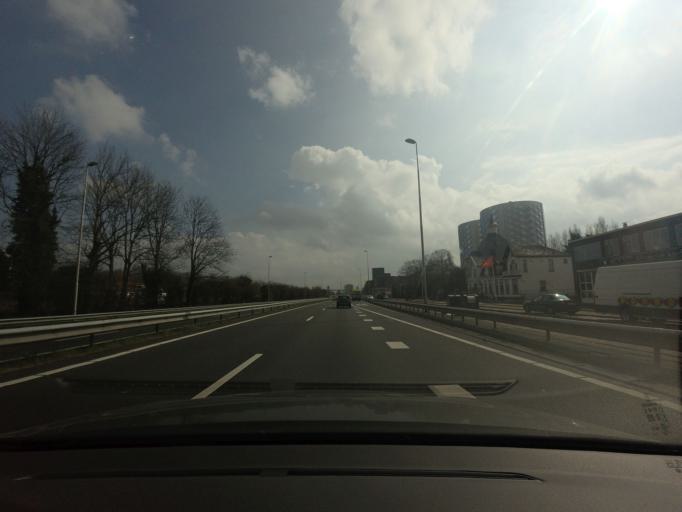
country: NL
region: North Holland
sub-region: Gemeente Zaanstad
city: Zaanstad
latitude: 52.3862
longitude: 4.7423
